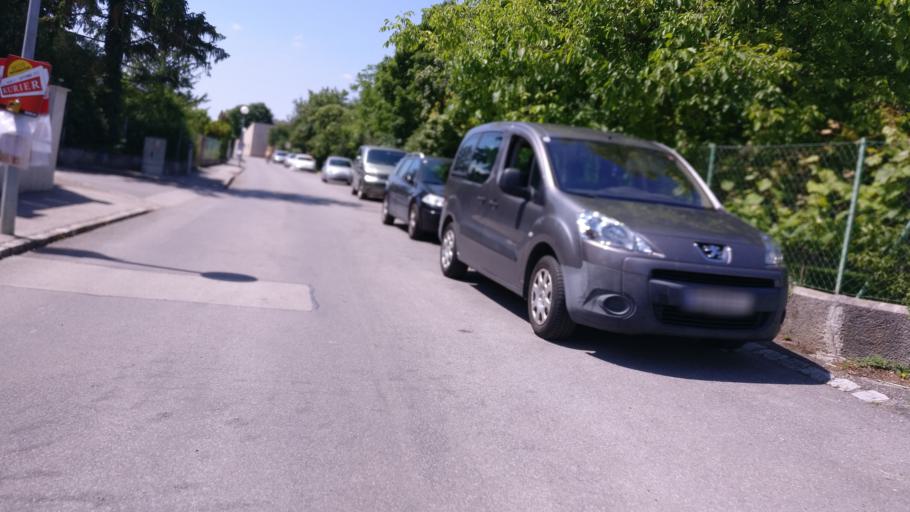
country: AT
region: Lower Austria
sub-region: Politischer Bezirk Baden
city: Oberwaltersdorf
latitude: 47.9773
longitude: 16.3246
